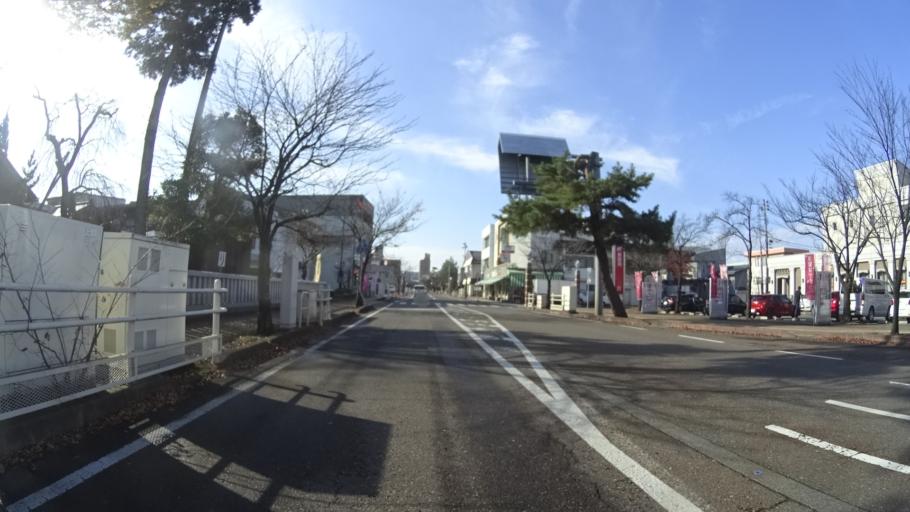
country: JP
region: Niigata
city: Joetsu
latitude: 37.1088
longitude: 138.2498
